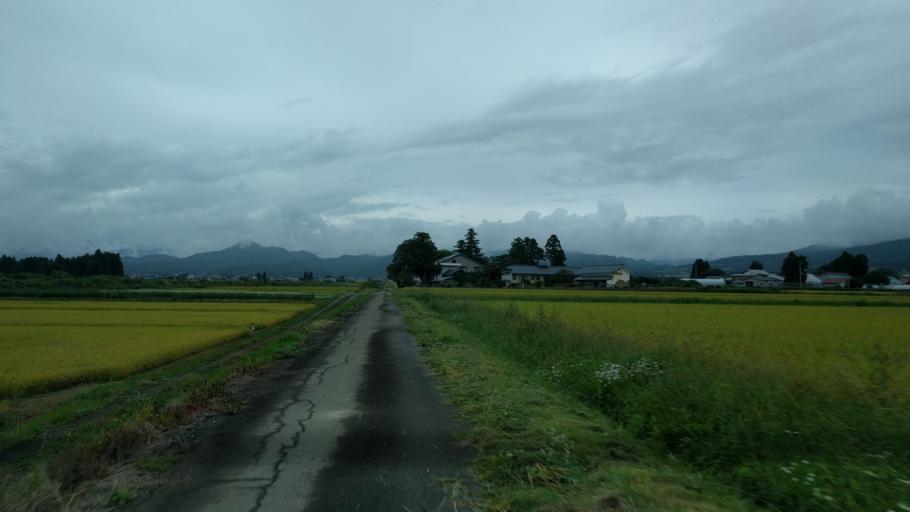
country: JP
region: Fukushima
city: Kitakata
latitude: 37.6236
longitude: 139.9102
